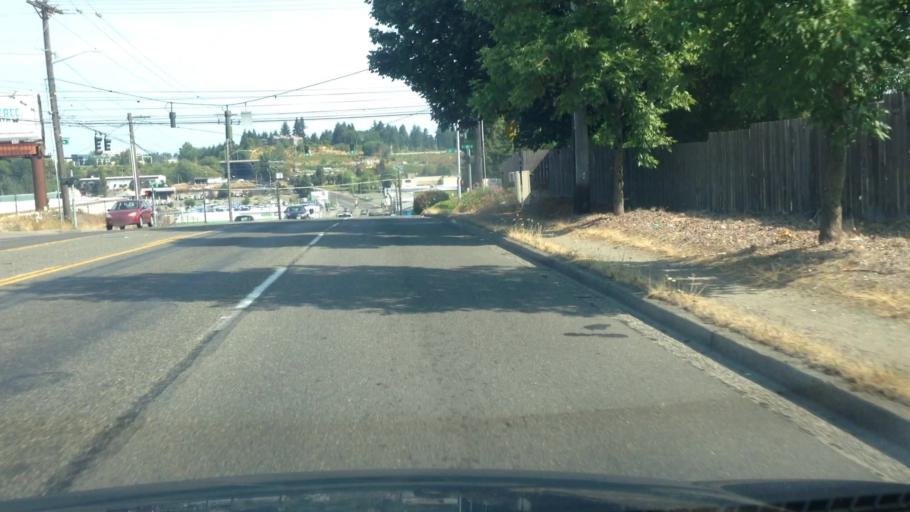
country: US
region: Washington
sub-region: Pierce County
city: Tacoma
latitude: 47.2277
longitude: -122.4735
